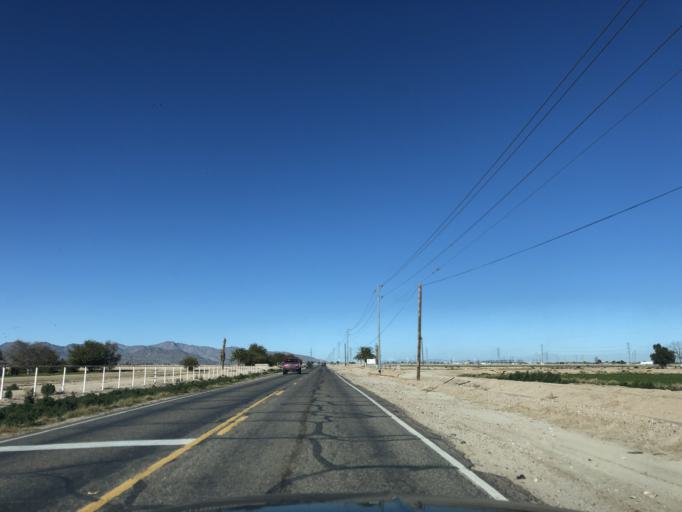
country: US
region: Arizona
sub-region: Maricopa County
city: Buckeye
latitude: 33.3978
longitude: -112.5042
